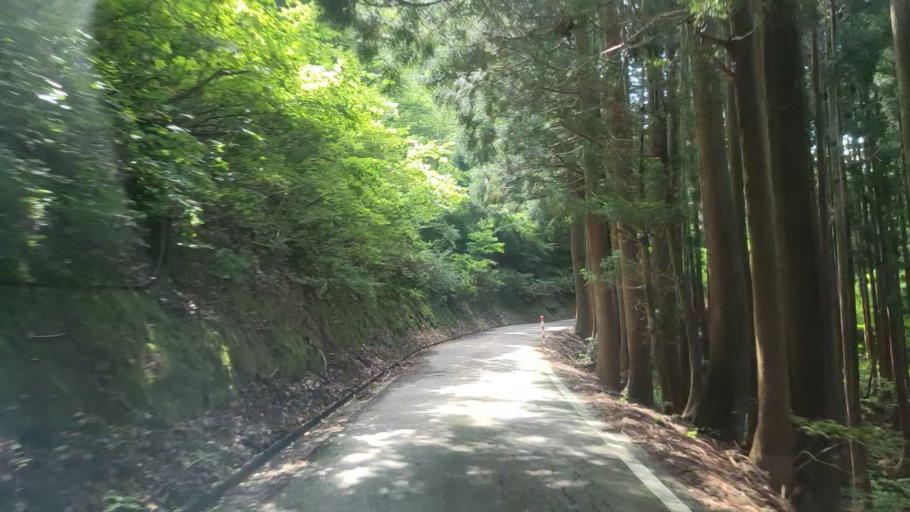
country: JP
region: Ishikawa
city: Komatsu
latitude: 36.2768
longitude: 136.5342
